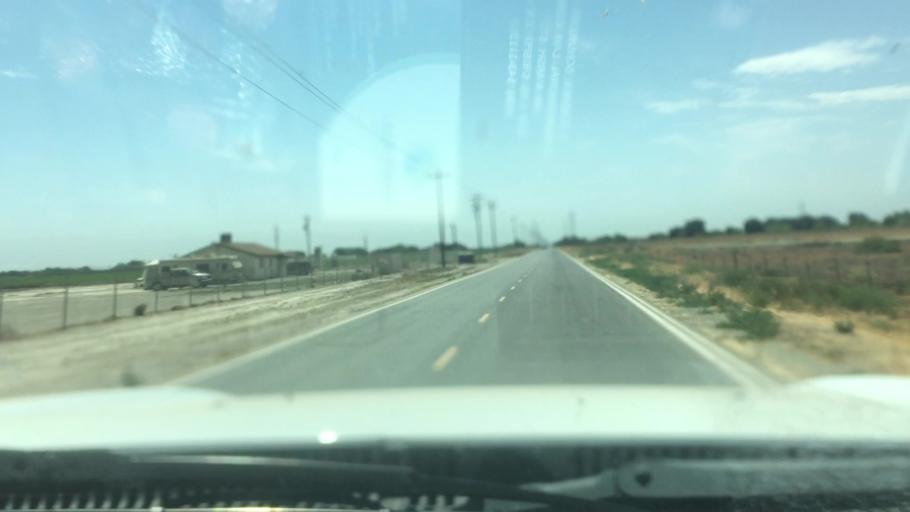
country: US
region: California
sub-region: Kings County
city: Corcoran
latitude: 36.0508
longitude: -119.4898
